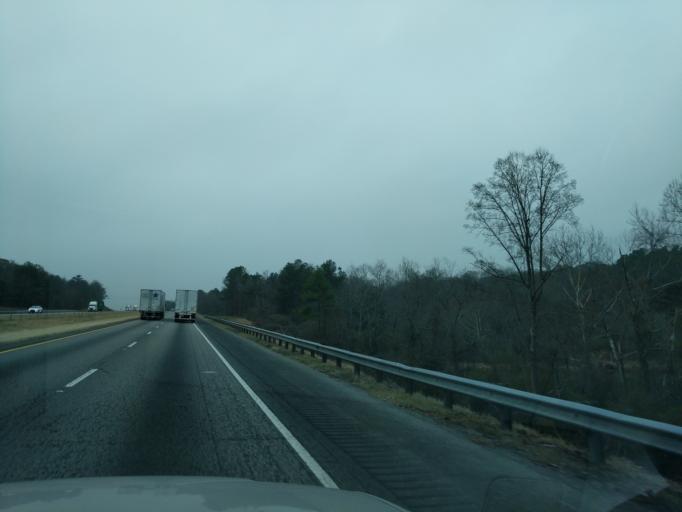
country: US
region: Georgia
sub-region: Banks County
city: Maysville
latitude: 34.2211
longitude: -83.5183
